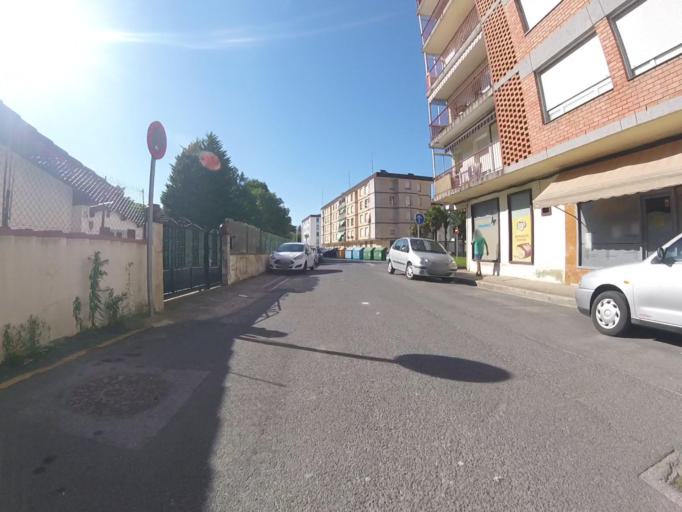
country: ES
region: Basque Country
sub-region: Provincia de Guipuzcoa
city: Irun
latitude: 43.3356
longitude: -1.7801
